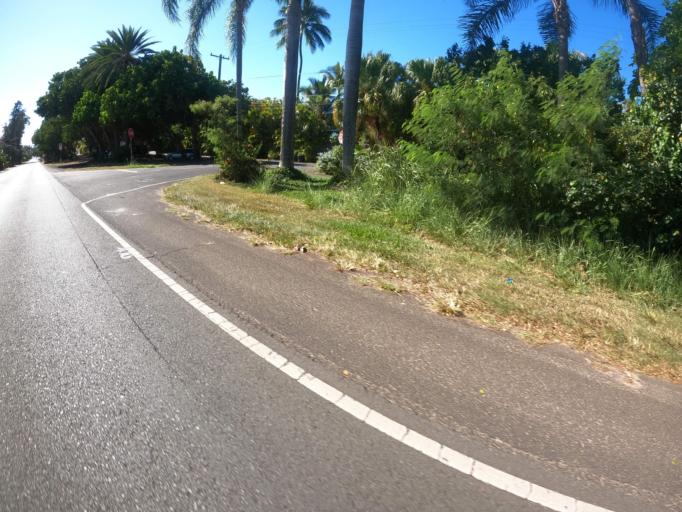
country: US
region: Hawaii
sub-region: Honolulu County
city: Pupukea
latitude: 21.6630
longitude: -158.0523
